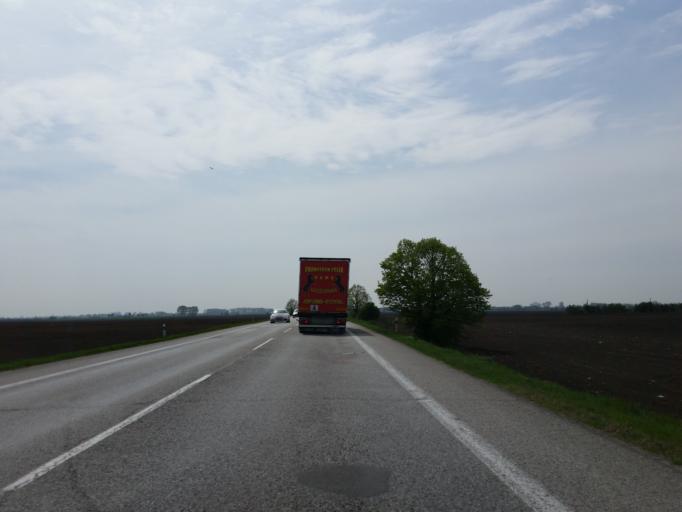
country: SK
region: Trnavsky
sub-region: Okres Galanta
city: Galanta
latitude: 48.2541
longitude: 17.7423
